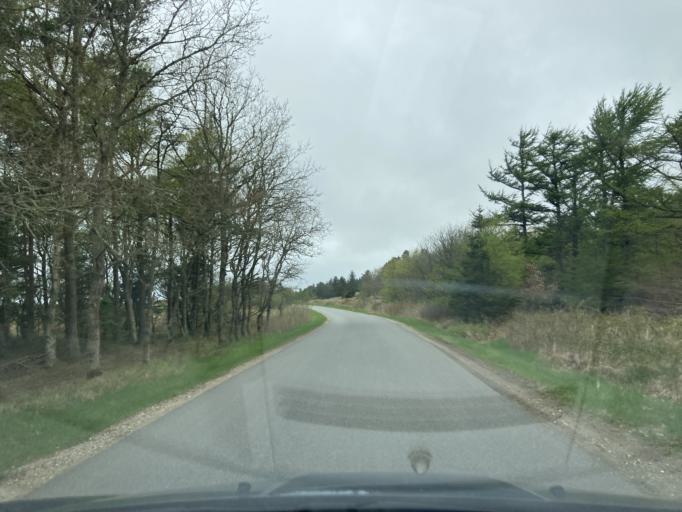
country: DK
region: North Denmark
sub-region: Thisted Kommune
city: Hurup
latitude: 56.8165
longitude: 8.2941
